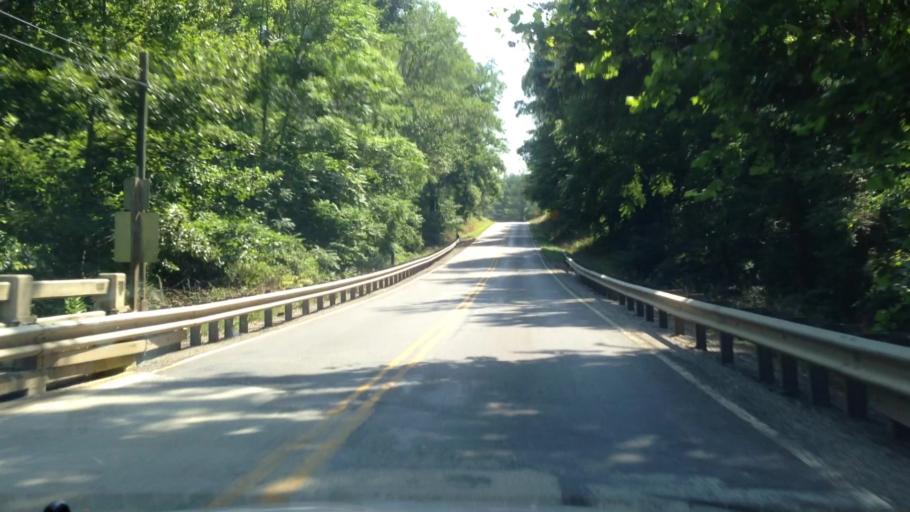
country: US
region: Virginia
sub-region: Patrick County
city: Stuart
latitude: 36.5949
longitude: -80.3126
